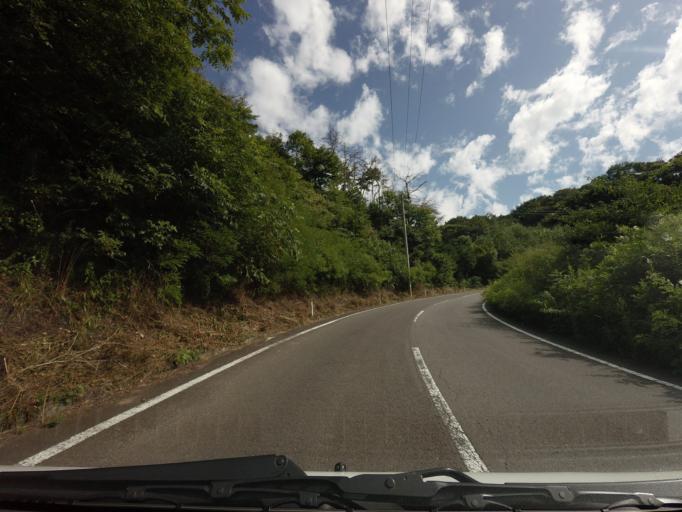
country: JP
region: Fukushima
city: Nihommatsu
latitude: 37.6333
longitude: 140.4146
